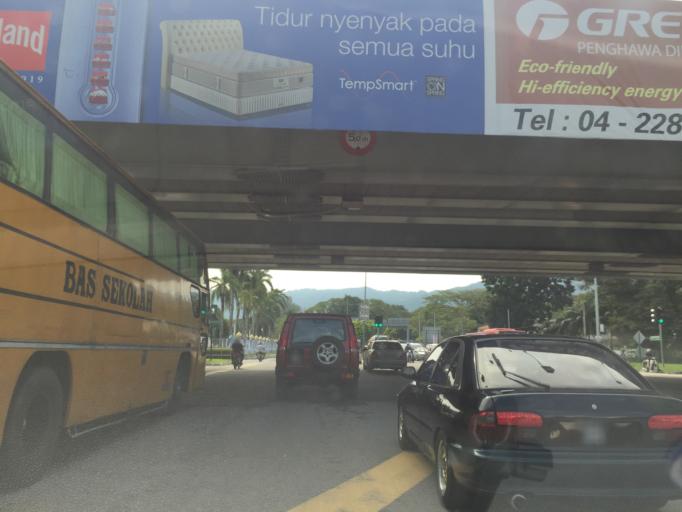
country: MY
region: Penang
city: George Town
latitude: 5.4079
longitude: 100.3028
